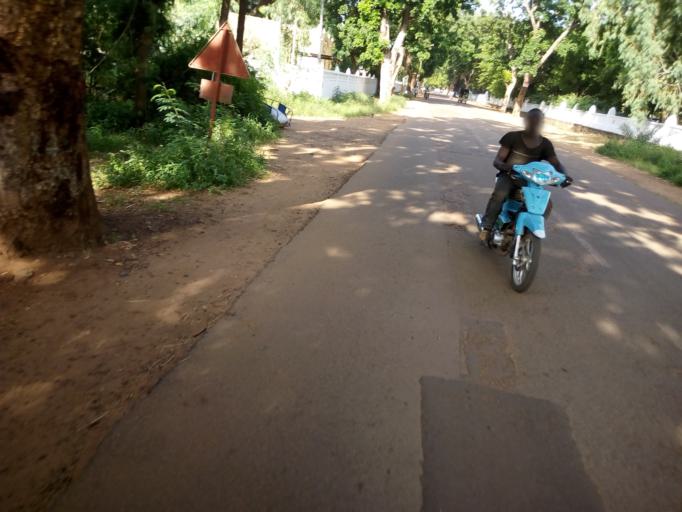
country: ML
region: Segou
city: Segou
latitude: 13.4391
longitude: -6.2819
